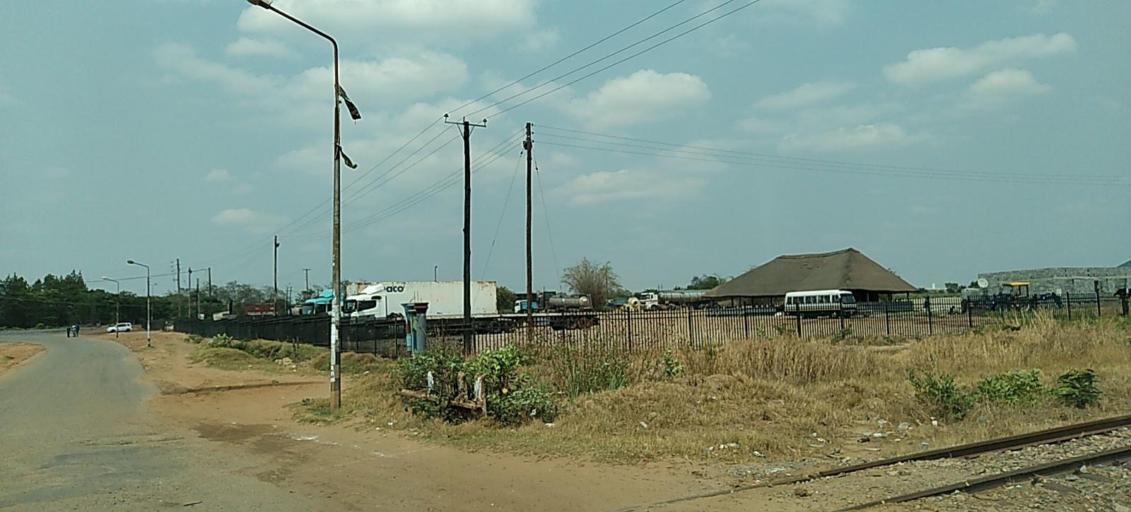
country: ZM
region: Copperbelt
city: Chambishi
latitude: -12.6431
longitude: 28.0566
